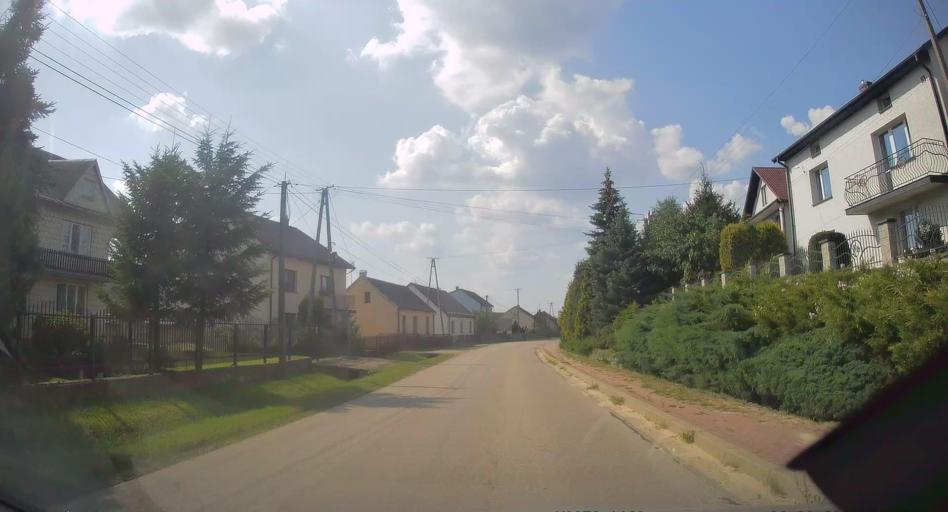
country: PL
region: Swietokrzyskie
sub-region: Powiat kielecki
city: Checiny
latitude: 50.8163
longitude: 20.4025
